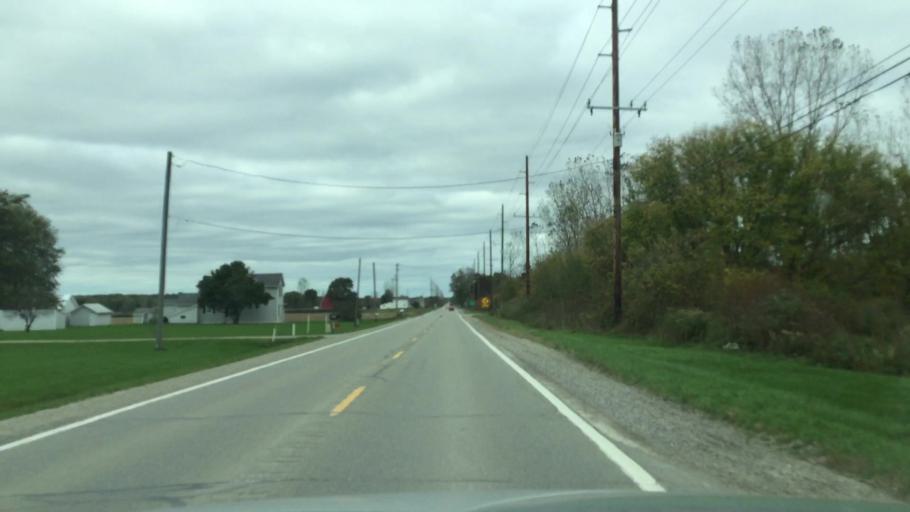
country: US
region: Michigan
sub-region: Macomb County
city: Richmond
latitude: 42.8082
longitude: -82.8003
